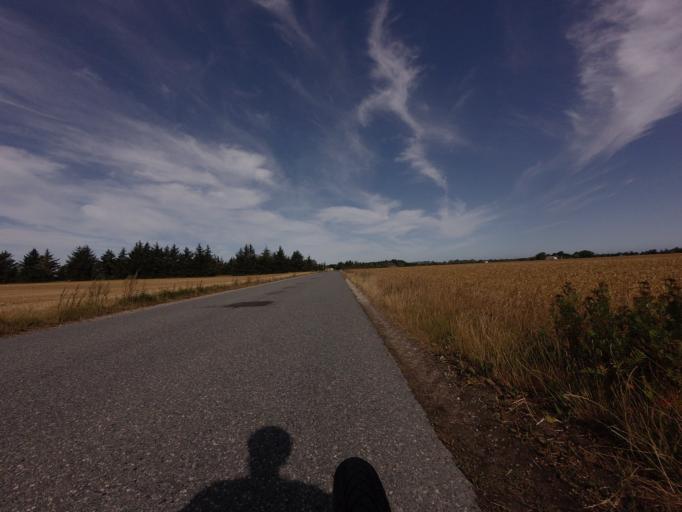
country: DK
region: North Denmark
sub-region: Hjorring Kommune
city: Vra
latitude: 57.4204
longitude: 9.8556
